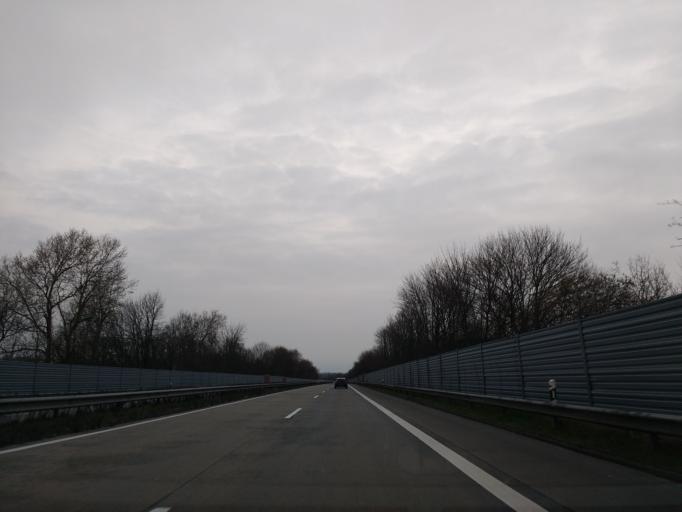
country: DE
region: Lower Saxony
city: Midlum
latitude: 53.7561
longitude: 8.6820
